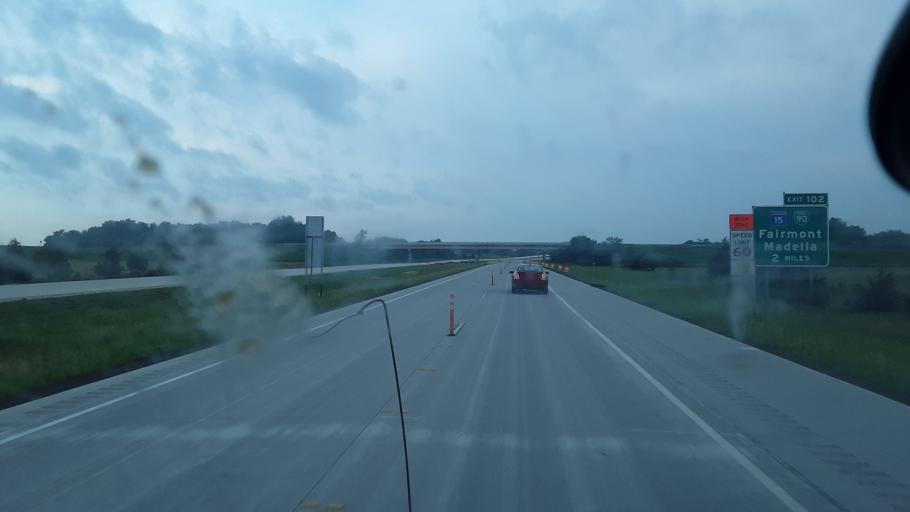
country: US
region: Minnesota
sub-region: Martin County
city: Fairmont
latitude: 43.6709
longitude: -94.4042
